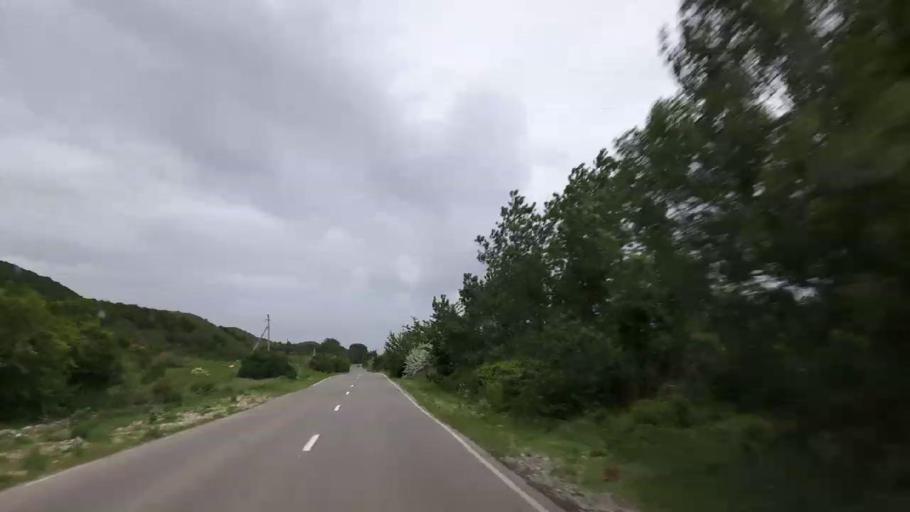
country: GE
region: Shida Kartli
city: Gori
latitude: 41.9926
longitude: 44.0323
